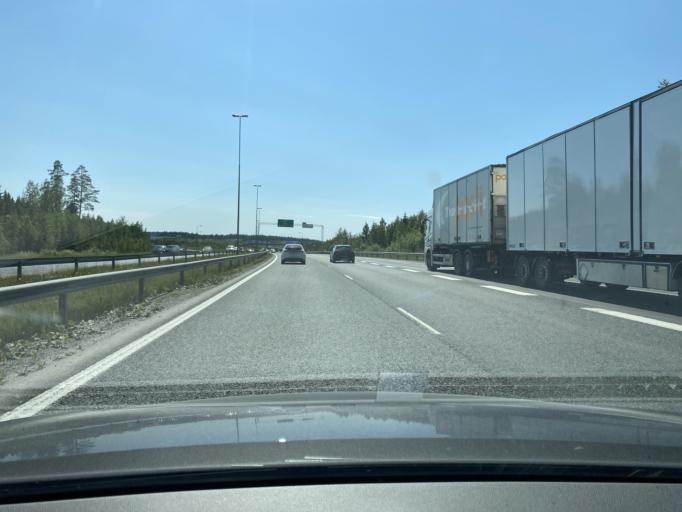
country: FI
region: Pirkanmaa
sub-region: Tampere
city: Pirkkala
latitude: 61.4593
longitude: 23.6997
